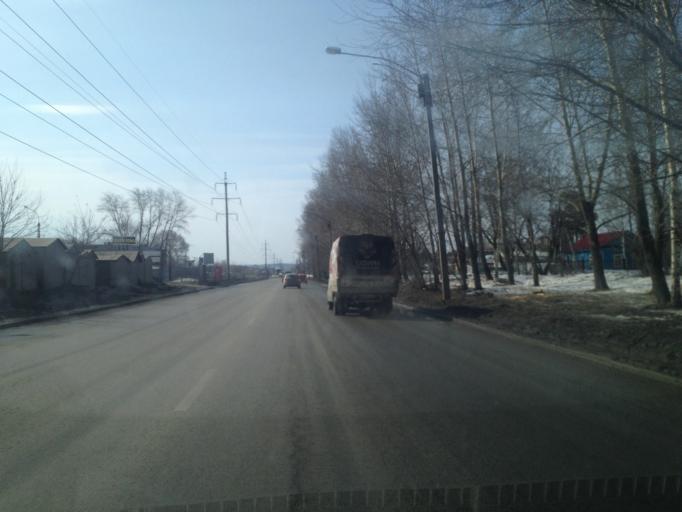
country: RU
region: Sverdlovsk
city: Sovkhoznyy
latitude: 56.7678
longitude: 60.5942
